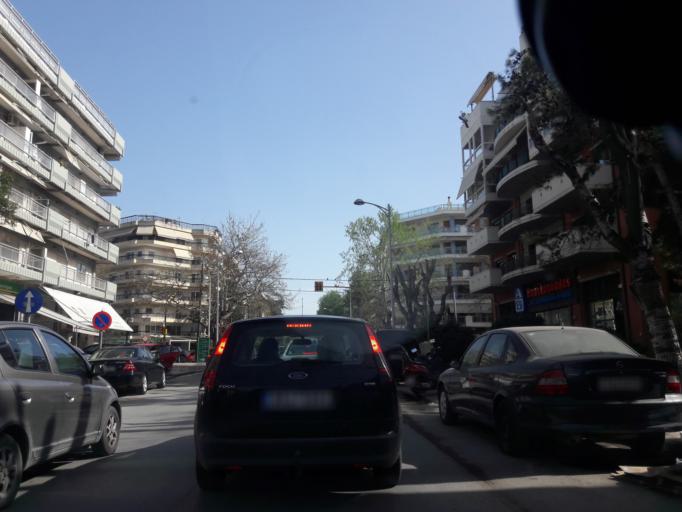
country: GR
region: Central Macedonia
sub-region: Nomos Thessalonikis
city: Kalamaria
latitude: 40.5934
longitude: 22.9497
